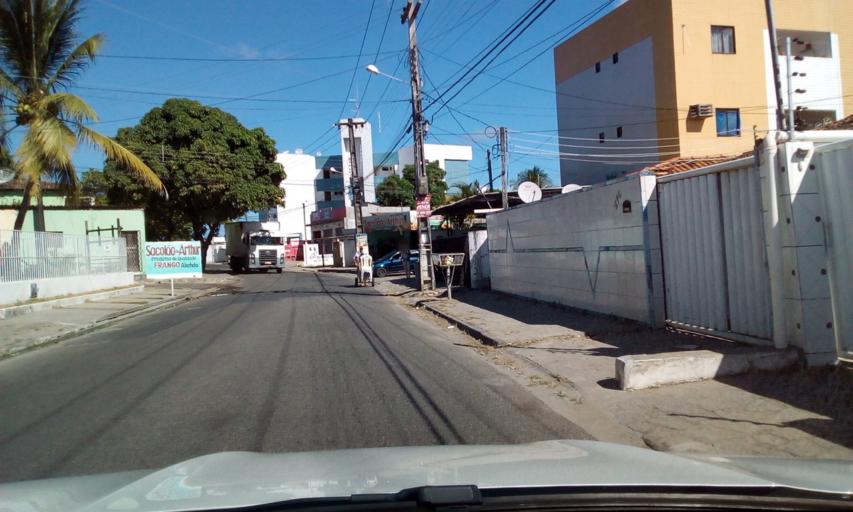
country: BR
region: Paraiba
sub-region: Joao Pessoa
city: Joao Pessoa
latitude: -7.1812
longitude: -34.8621
